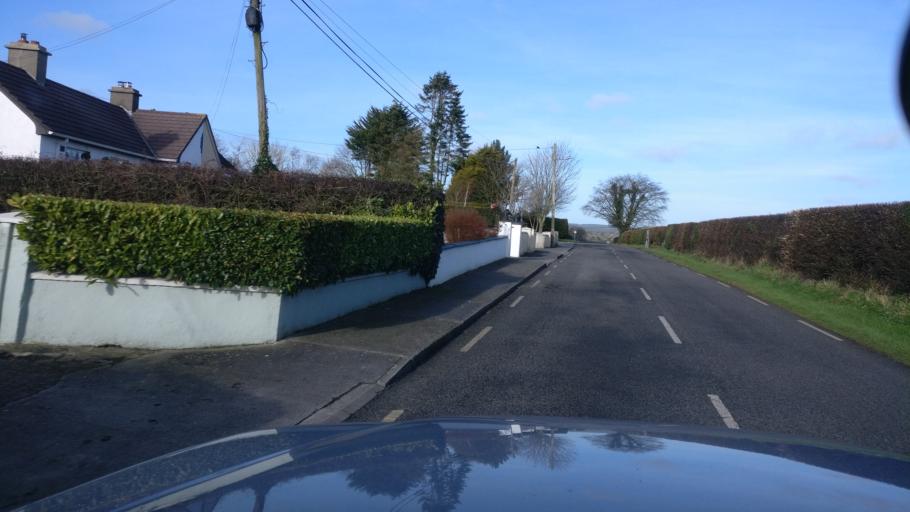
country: IE
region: Leinster
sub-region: Kilkenny
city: Castlecomer
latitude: 52.8704
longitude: -7.1643
